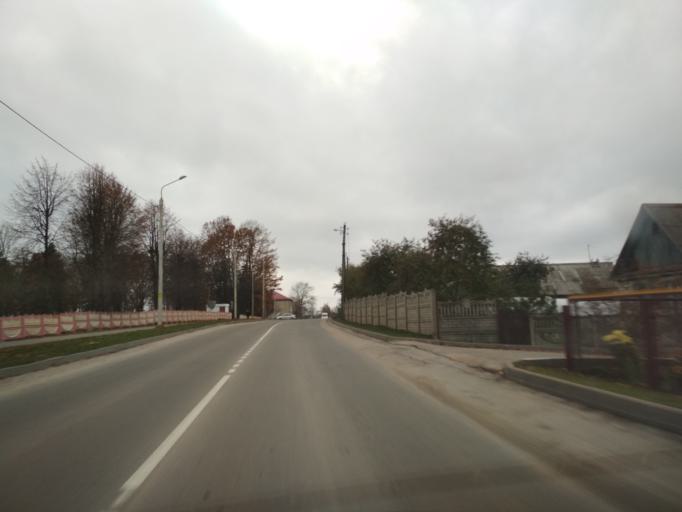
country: BY
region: Minsk
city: Mar''ina Horka
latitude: 53.5194
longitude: 28.1570
